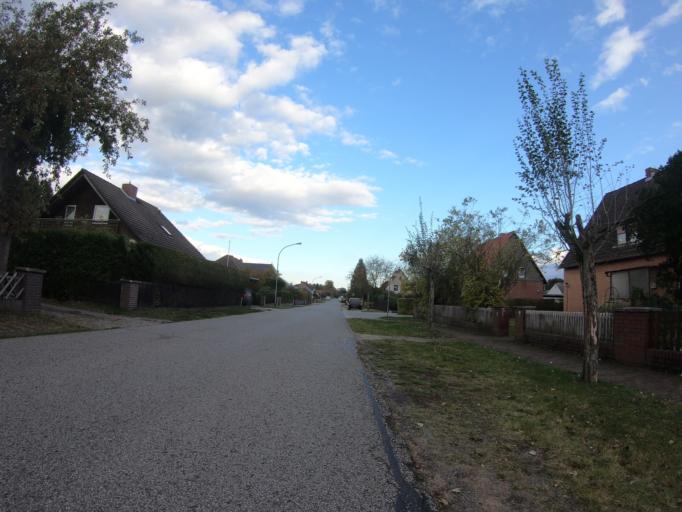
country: DE
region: Lower Saxony
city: Wagenhoff
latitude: 52.5536
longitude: 10.5180
